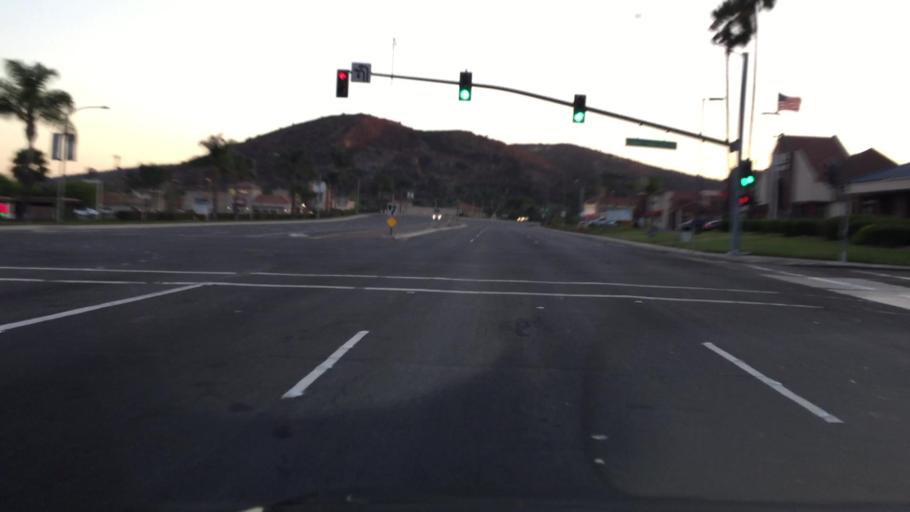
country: US
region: California
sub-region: San Diego County
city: Rancho San Diego
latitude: 32.7411
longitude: -116.9386
